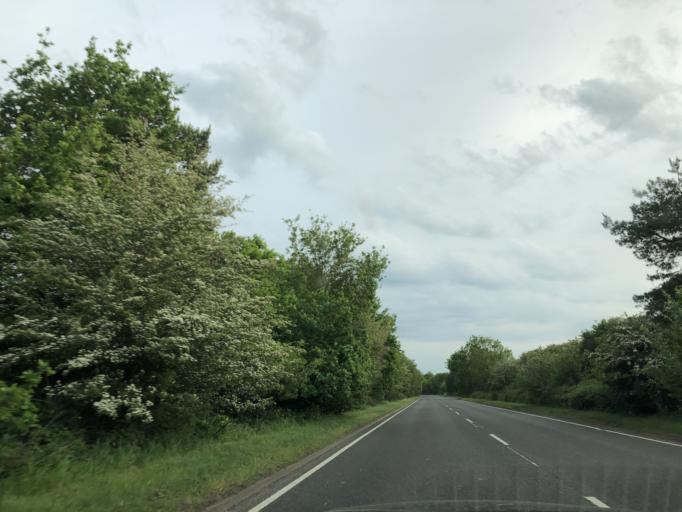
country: GB
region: England
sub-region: Warwickshire
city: Wroxall
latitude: 52.3437
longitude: -1.6555
